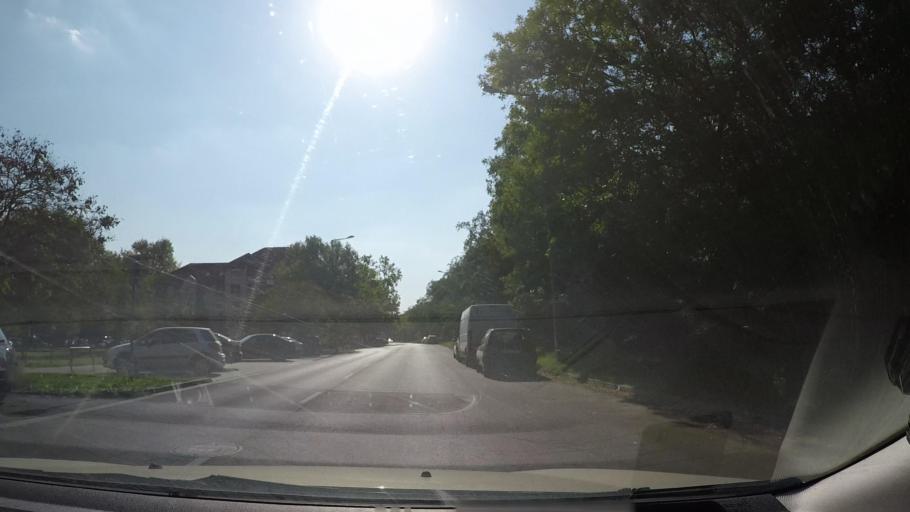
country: HU
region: Budapest
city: Budapest XV. keruelet
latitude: 47.5866
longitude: 19.1110
